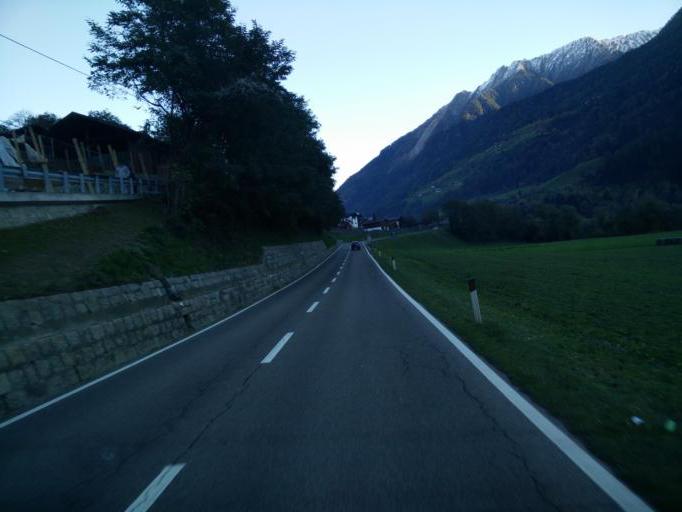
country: IT
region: Trentino-Alto Adige
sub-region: Bolzano
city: San Martino in Passiria
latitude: 46.7634
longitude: 11.2109
